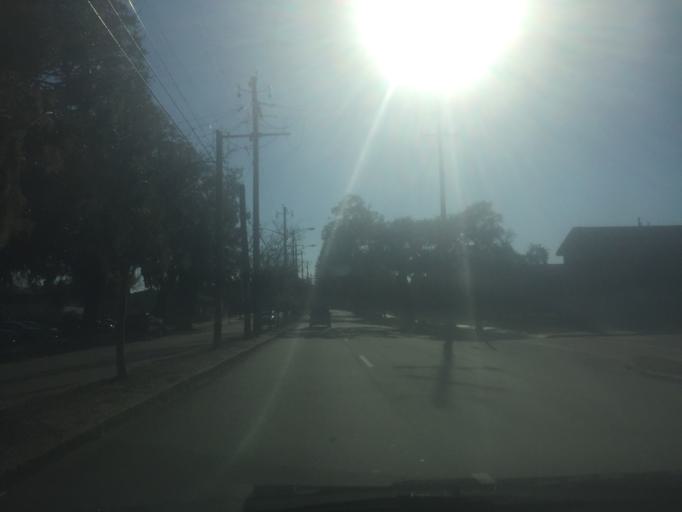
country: US
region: Georgia
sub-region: Chatham County
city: Savannah
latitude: 32.0662
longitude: -81.1027
